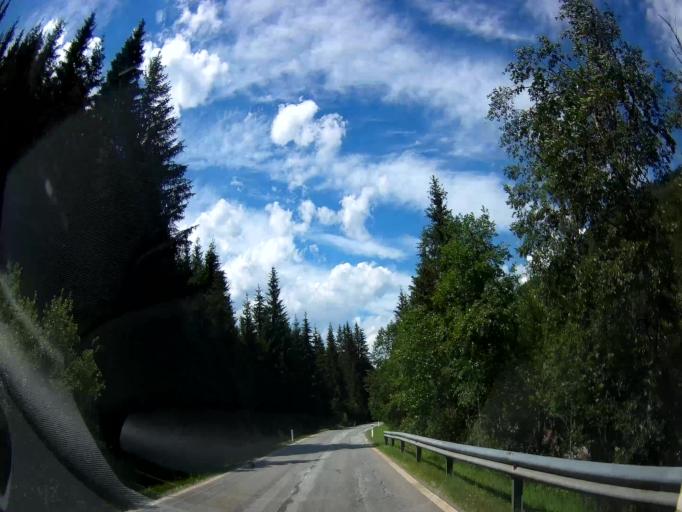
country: AT
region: Styria
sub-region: Politischer Bezirk Murau
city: Stadl an der Mur
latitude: 47.0068
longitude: 14.0098
